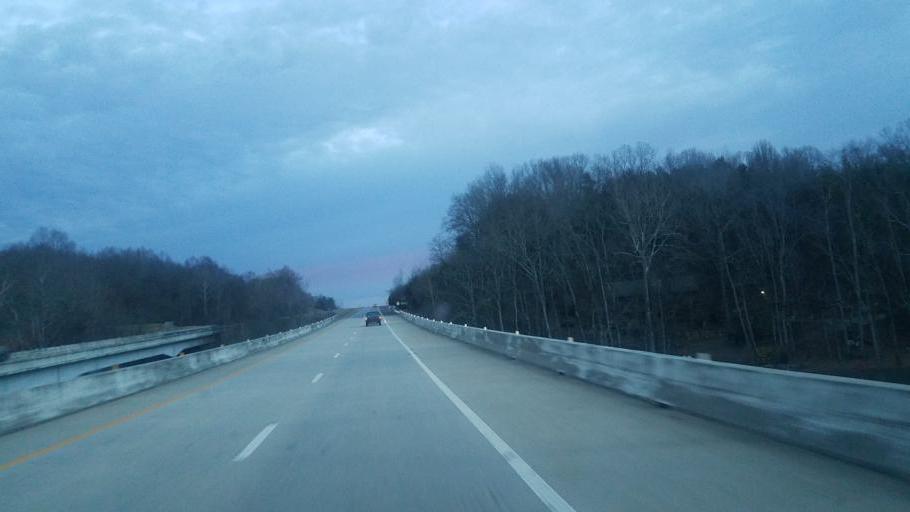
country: US
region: Tennessee
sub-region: Van Buren County
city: Spencer
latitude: 35.8211
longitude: -85.4610
